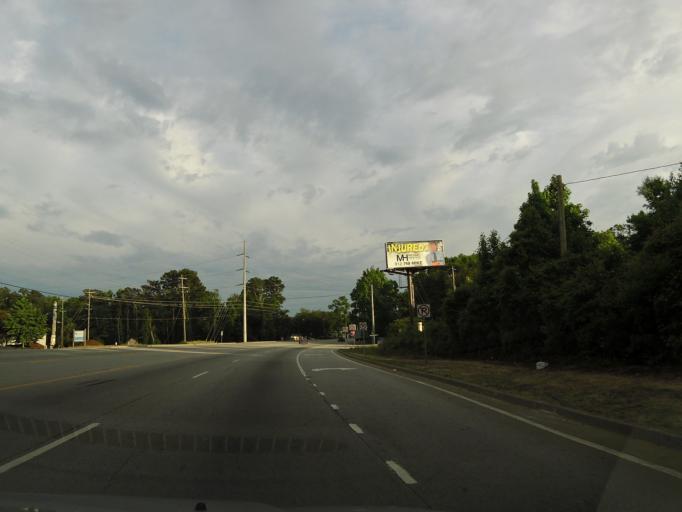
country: US
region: Georgia
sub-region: Chatham County
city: Garden City
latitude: 32.0834
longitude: -81.1962
